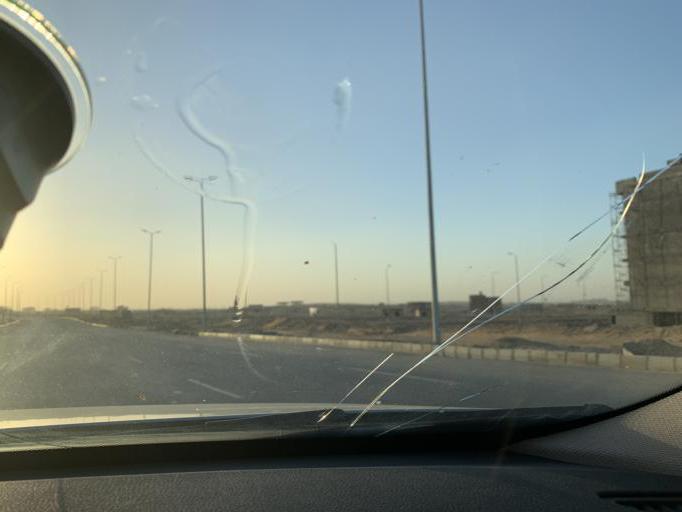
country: EG
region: Muhafazat al Qalyubiyah
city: Al Khankah
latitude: 30.0243
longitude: 31.5893
